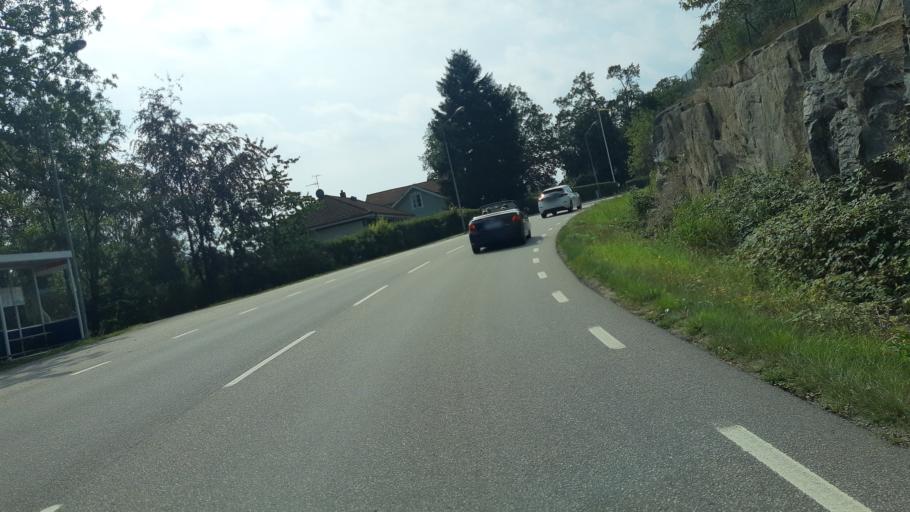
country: SE
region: Blekinge
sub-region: Karlskrona Kommun
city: Nattraby
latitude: 56.1940
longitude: 15.5356
